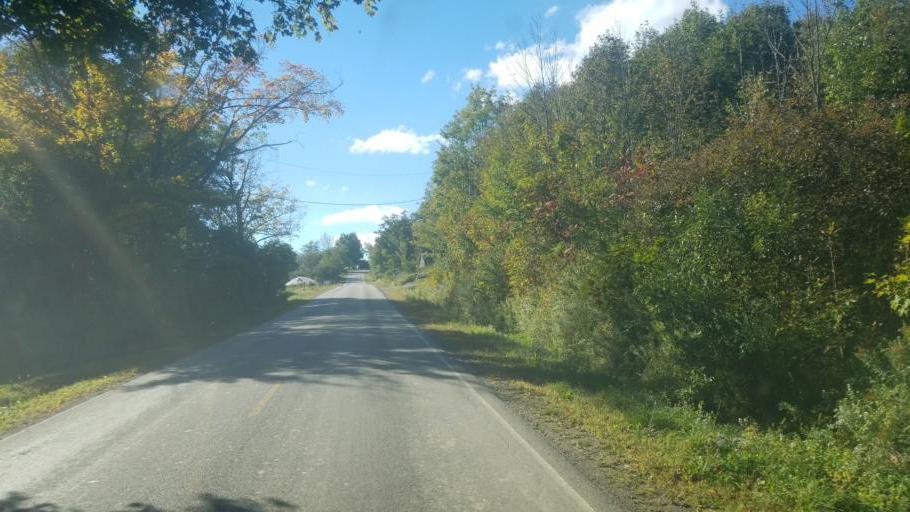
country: US
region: New York
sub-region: Allegany County
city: Friendship
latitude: 42.2757
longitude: -78.1495
